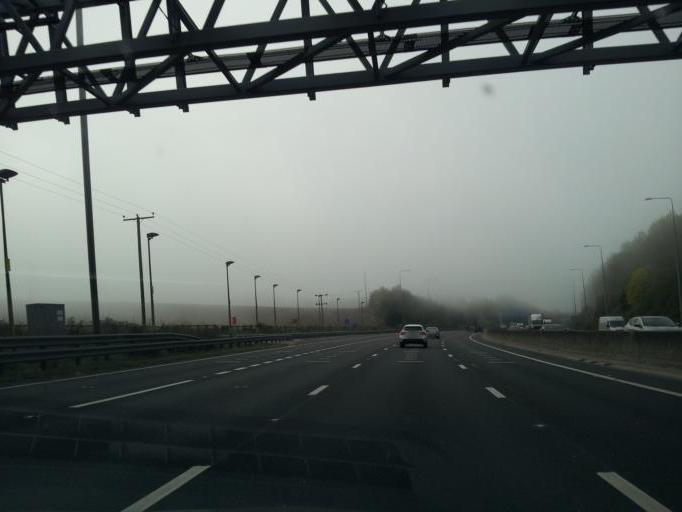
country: GB
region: England
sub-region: Kirklees
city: Cleckheaton
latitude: 53.7052
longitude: -1.7431
